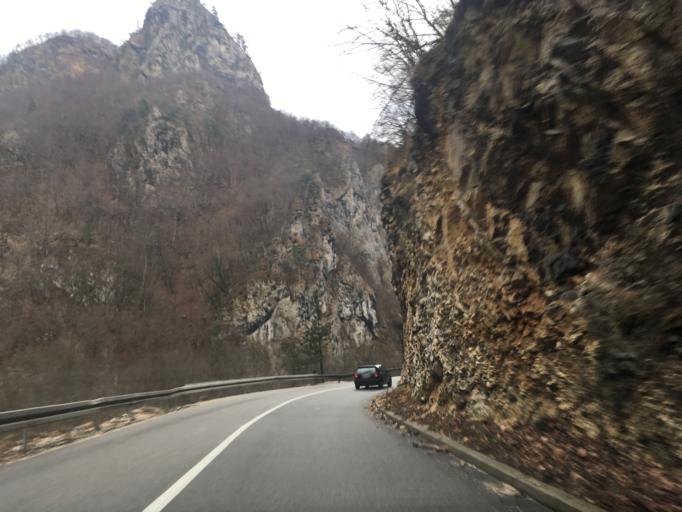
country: RS
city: Sokolovo Brdo
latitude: 43.1710
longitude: 19.7730
